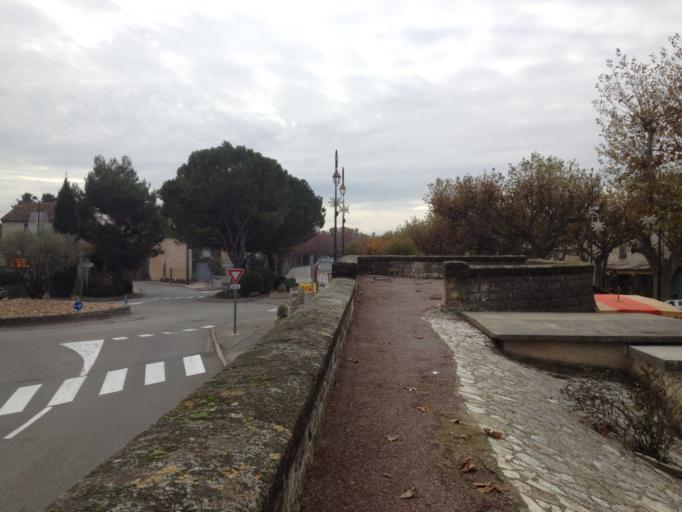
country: FR
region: Provence-Alpes-Cote d'Azur
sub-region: Departement du Vaucluse
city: Caderousse
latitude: 44.1029
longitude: 4.7585
